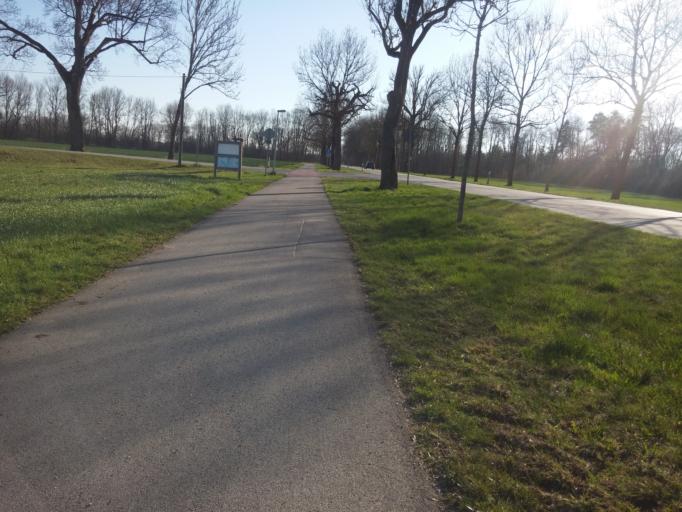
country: DE
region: Bavaria
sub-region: Upper Bavaria
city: Ismaning
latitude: 48.2490
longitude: 11.6917
